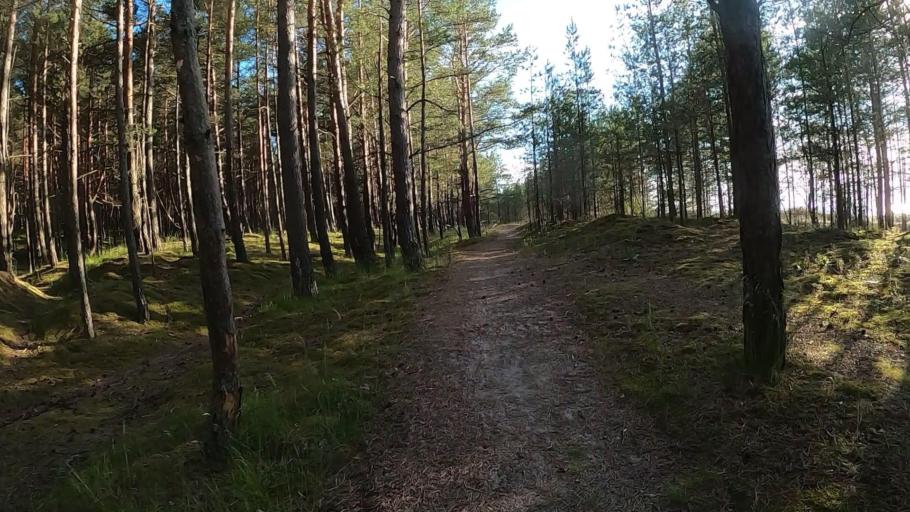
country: LV
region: Carnikava
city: Carnikava
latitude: 57.1192
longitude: 24.2021
